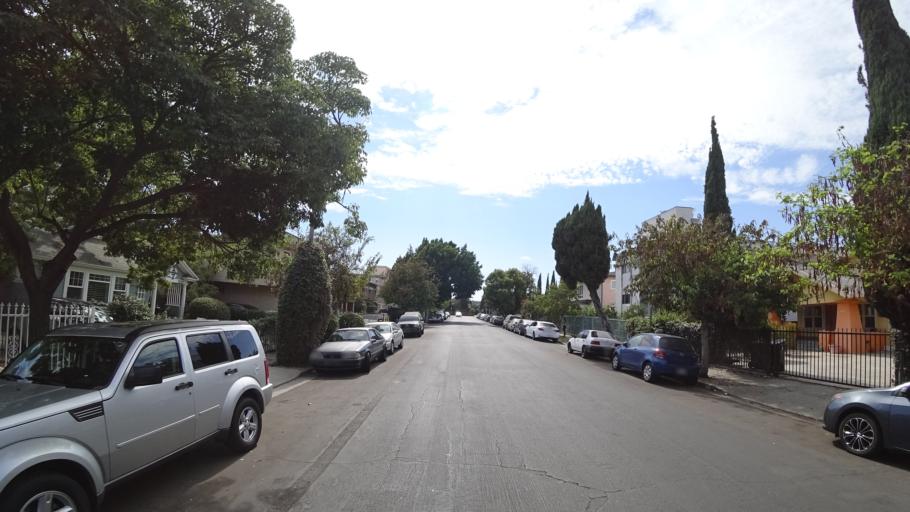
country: US
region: California
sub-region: Los Angeles County
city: Hollywood
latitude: 34.0929
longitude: -118.3164
